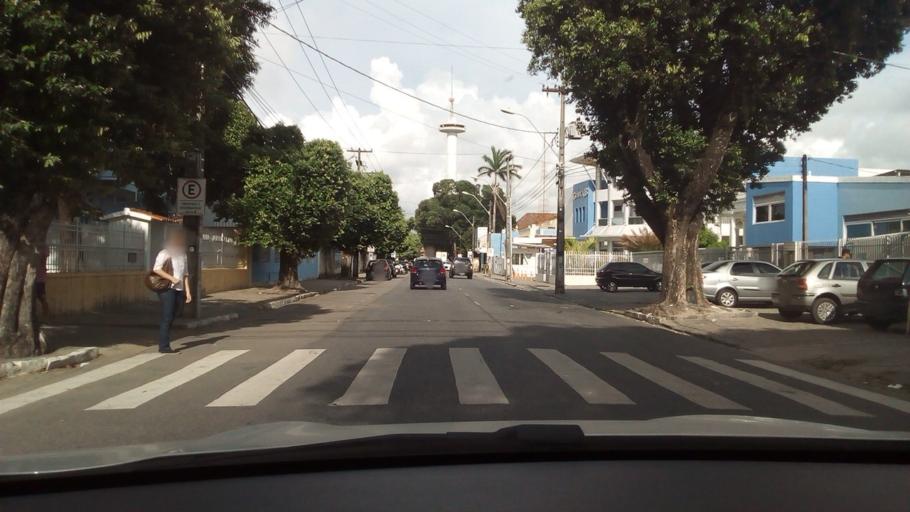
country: BR
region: Paraiba
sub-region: Joao Pessoa
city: Joao Pessoa
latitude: -7.1180
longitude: -34.8716
